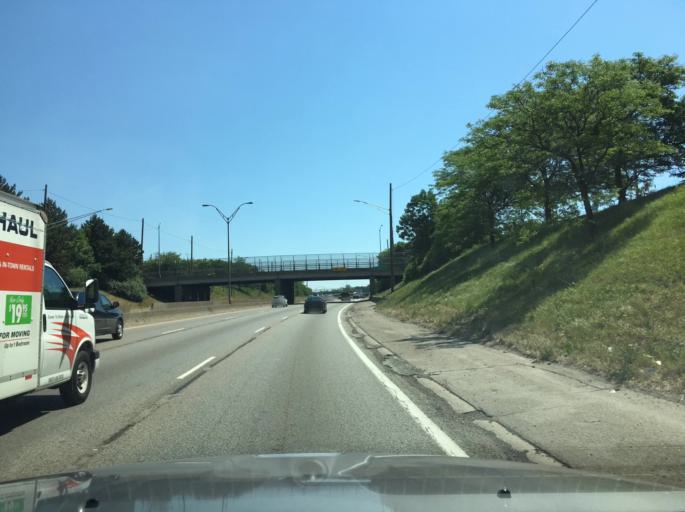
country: US
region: Michigan
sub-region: Wayne County
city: Hamtramck
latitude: 42.3844
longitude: -83.0276
